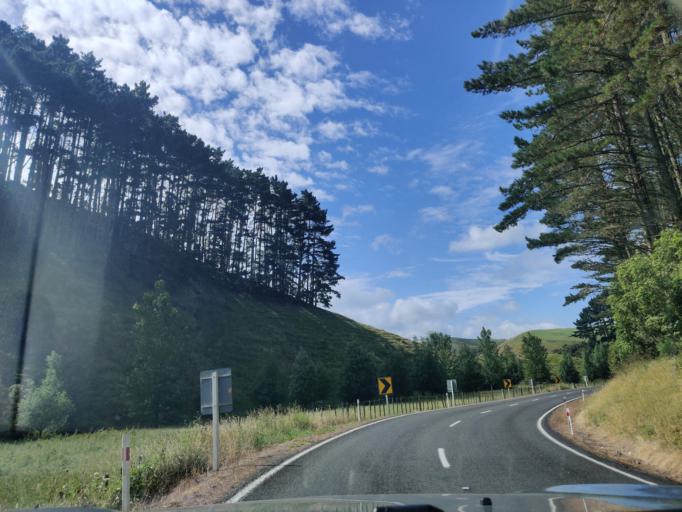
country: NZ
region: Waikato
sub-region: Otorohanga District
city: Otorohanga
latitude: -38.0974
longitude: 175.1311
